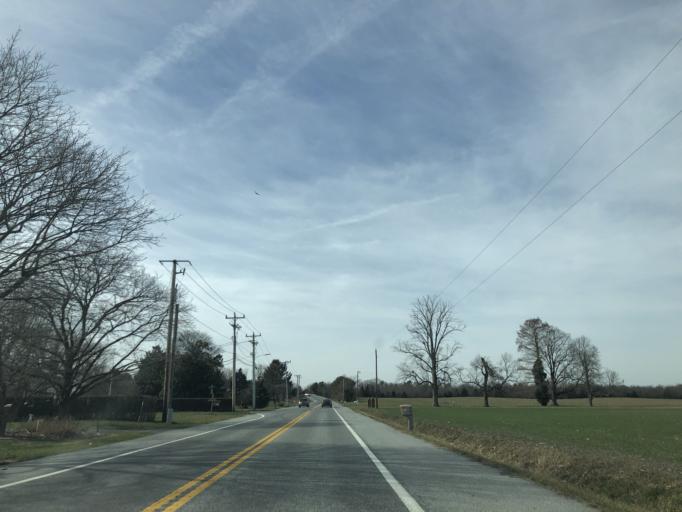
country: US
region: Delaware
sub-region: Kent County
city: Smyrna
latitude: 39.2907
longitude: -75.5865
